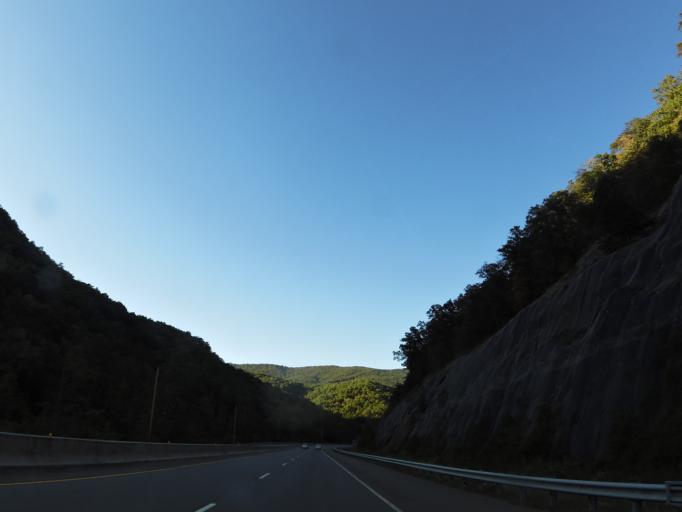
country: US
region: Tennessee
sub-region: Grainger County
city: Bean Station
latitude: 36.3492
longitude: -83.3376
